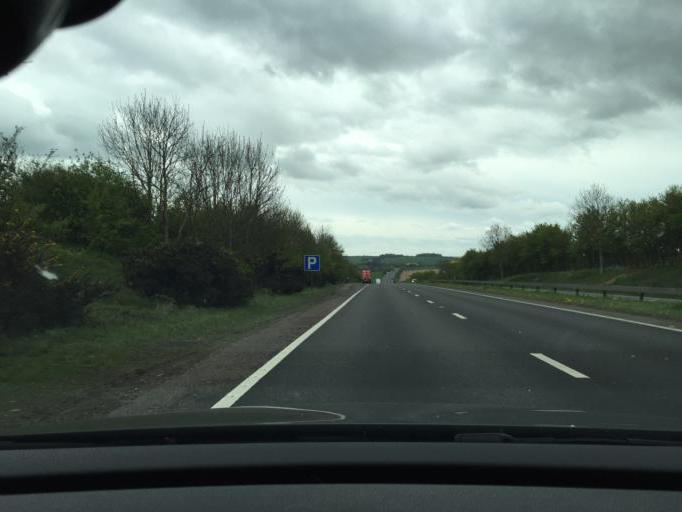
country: GB
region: England
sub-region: Oxfordshire
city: Harwell
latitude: 51.5441
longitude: -1.2936
